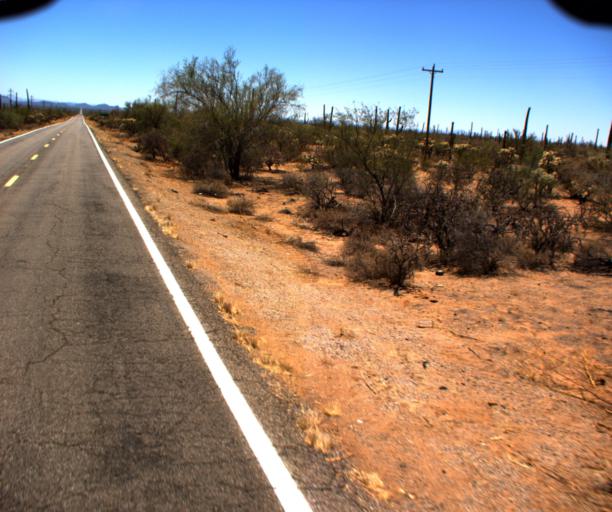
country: US
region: Arizona
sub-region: Pima County
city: Sells
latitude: 32.1216
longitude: -112.0828
